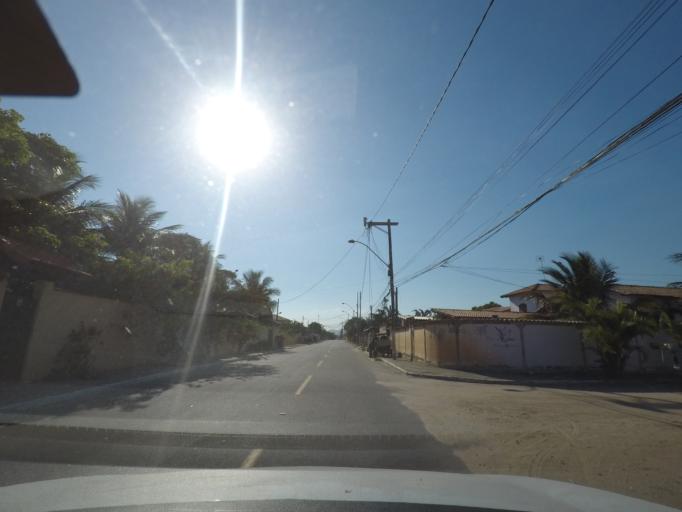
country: BR
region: Rio de Janeiro
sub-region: Marica
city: Marica
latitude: -22.9713
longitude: -42.9252
